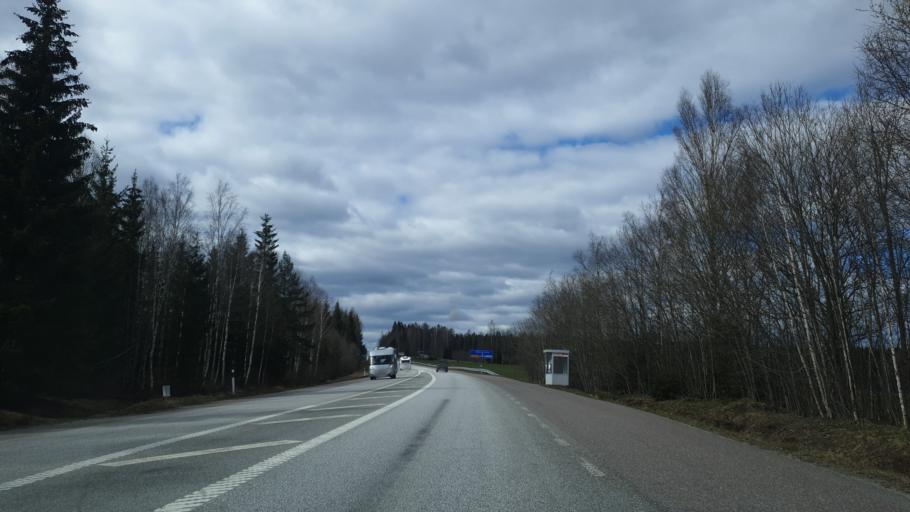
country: SE
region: OErebro
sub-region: Nora Kommun
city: Nora
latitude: 59.4908
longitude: 15.0589
